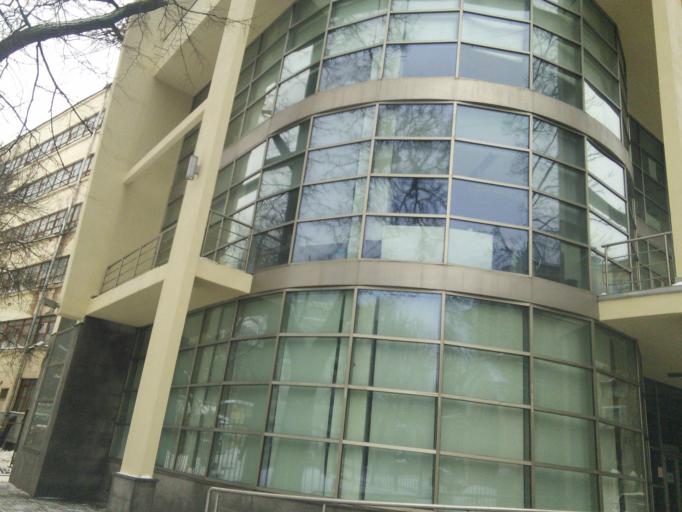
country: RU
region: Moscow
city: Moscow
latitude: 55.7656
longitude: 37.6419
